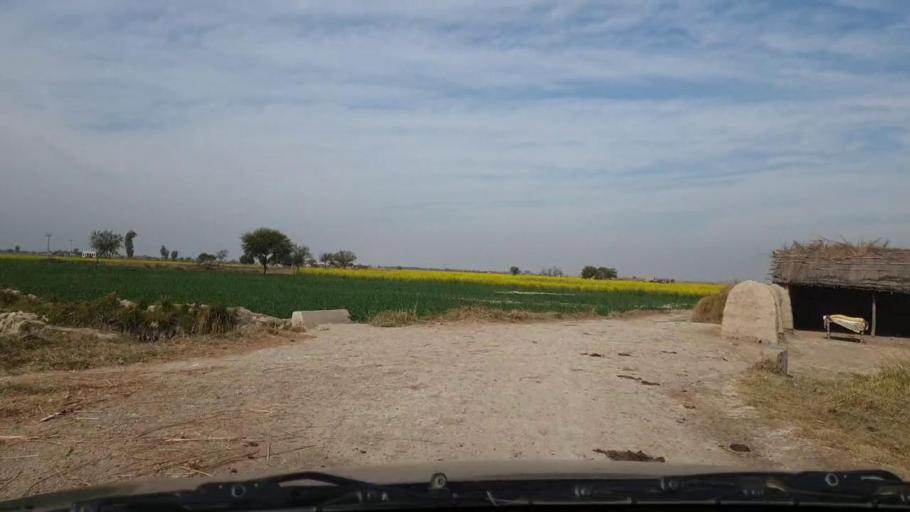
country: PK
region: Sindh
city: Jam Sahib
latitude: 26.2714
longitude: 68.7087
